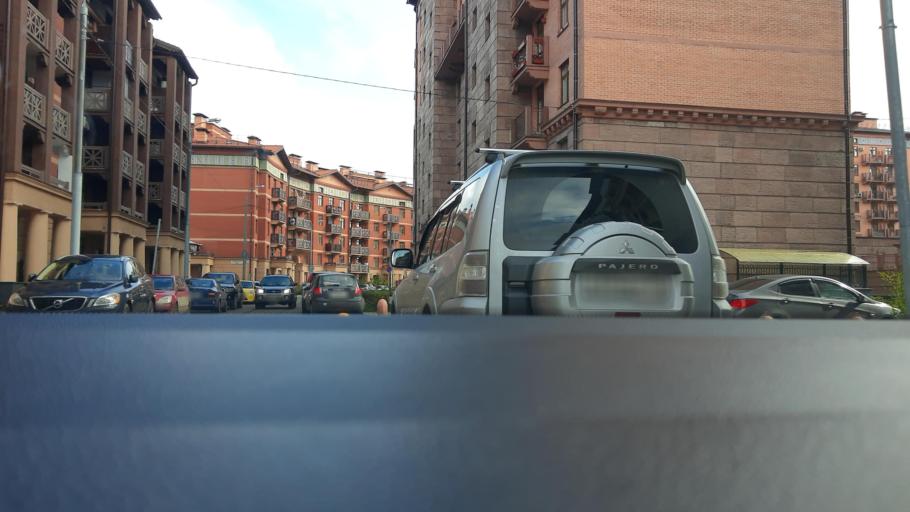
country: RU
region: Moskovskaya
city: Sheremet'yevskiy
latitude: 55.9593
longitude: 37.4407
